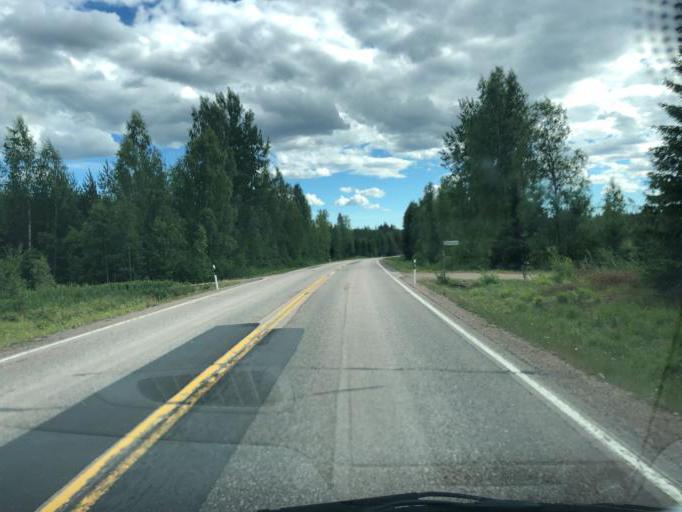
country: FI
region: Southern Savonia
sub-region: Mikkeli
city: Maentyharju
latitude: 61.1303
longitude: 27.1028
